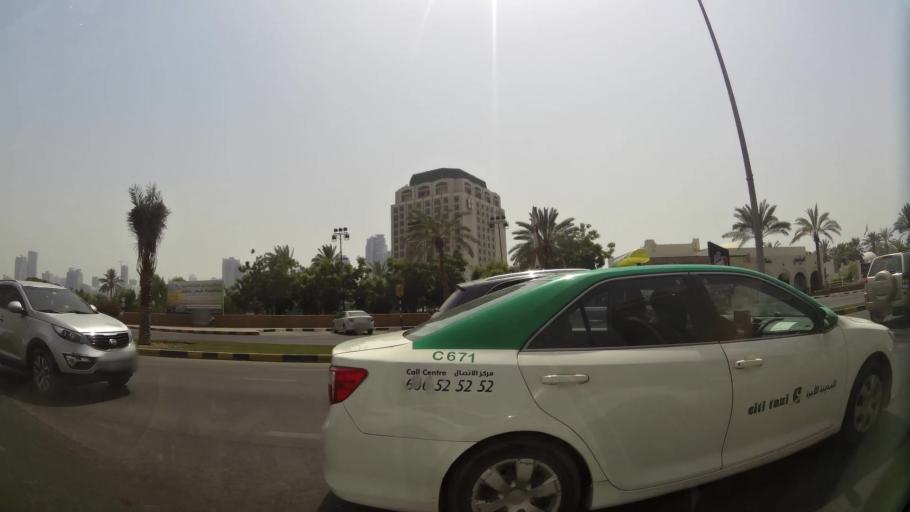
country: AE
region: Ash Shariqah
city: Sharjah
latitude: 25.3403
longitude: 55.3858
